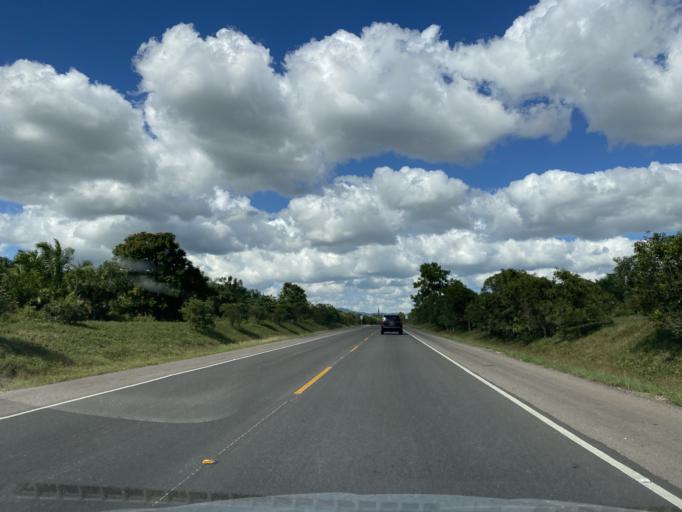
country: DO
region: Monte Plata
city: Monte Plata
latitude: 18.7362
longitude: -69.7626
